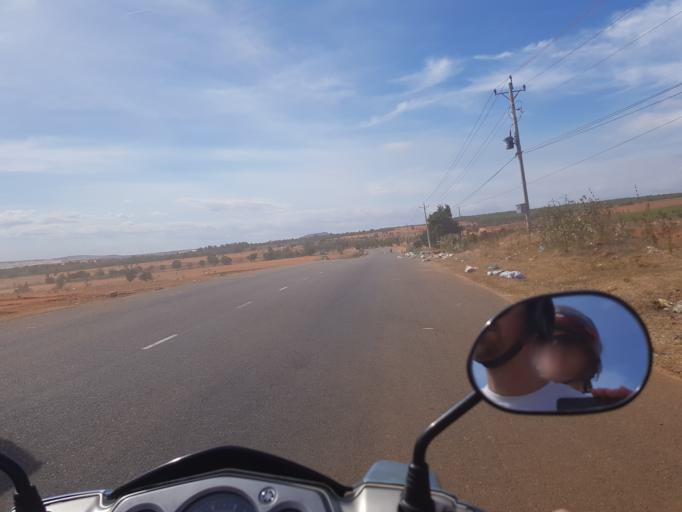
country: VN
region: Binh Thuan
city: Cho Lau
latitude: 11.0467
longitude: 108.3840
